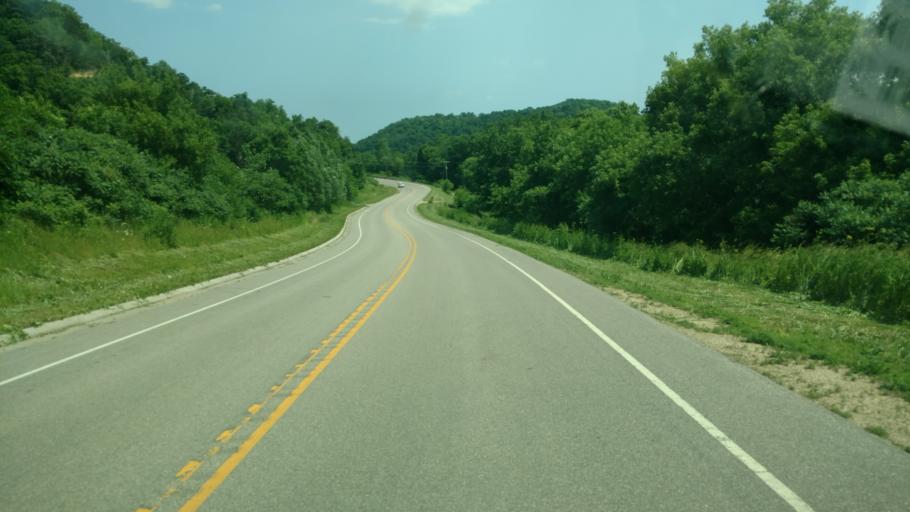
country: US
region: Wisconsin
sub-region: Vernon County
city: Viroqua
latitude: 43.4676
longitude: -90.7293
